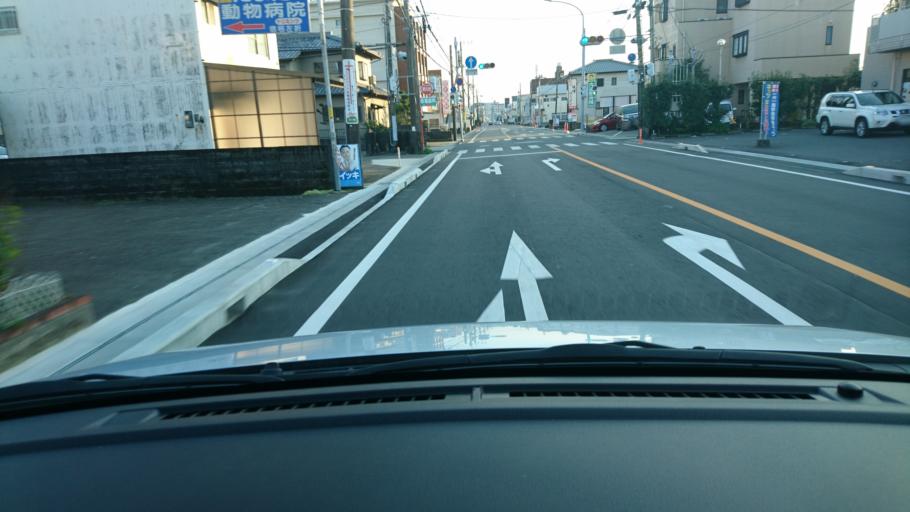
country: JP
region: Miyazaki
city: Miyazaki-shi
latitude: 31.9490
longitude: 131.4326
